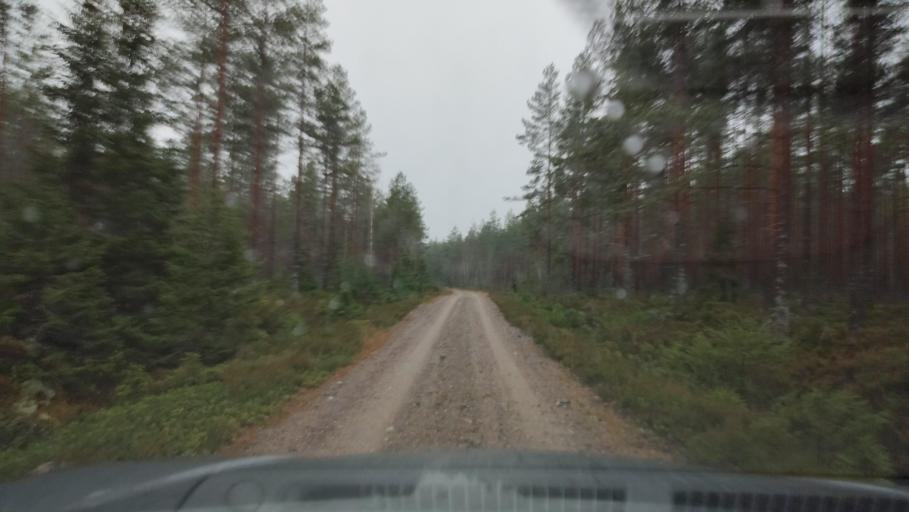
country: FI
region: Southern Ostrobothnia
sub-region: Suupohja
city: Karijoki
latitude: 62.1840
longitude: 21.7346
